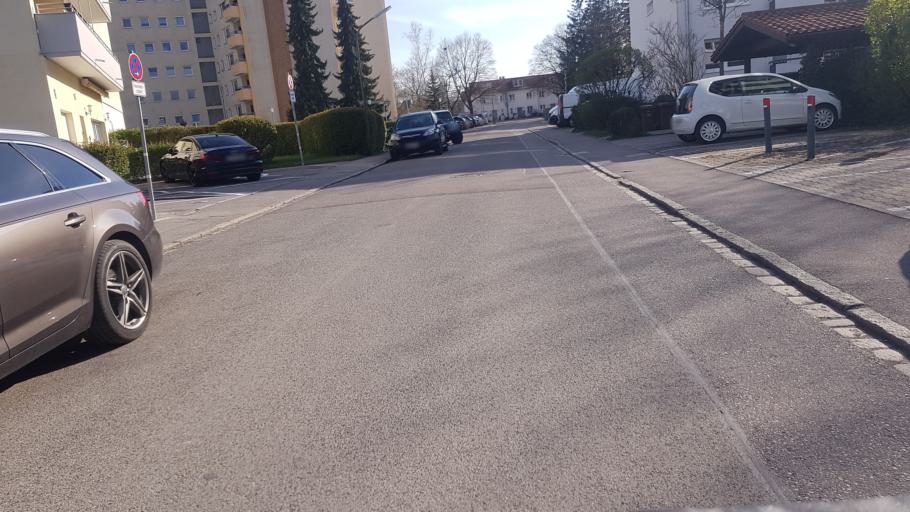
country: DE
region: Bavaria
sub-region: Upper Bavaria
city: Neuried
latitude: 48.0887
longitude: 11.4716
